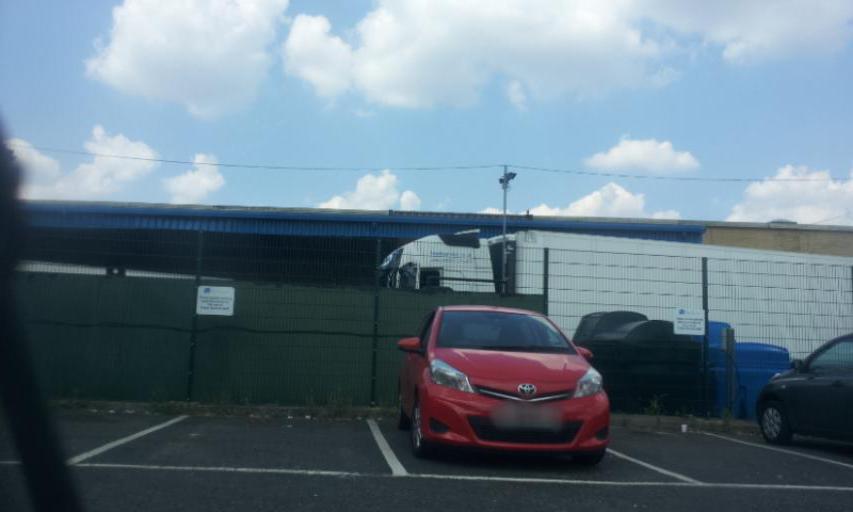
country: GB
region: England
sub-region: Kent
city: Paddock Wood
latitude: 51.1833
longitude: 0.3897
